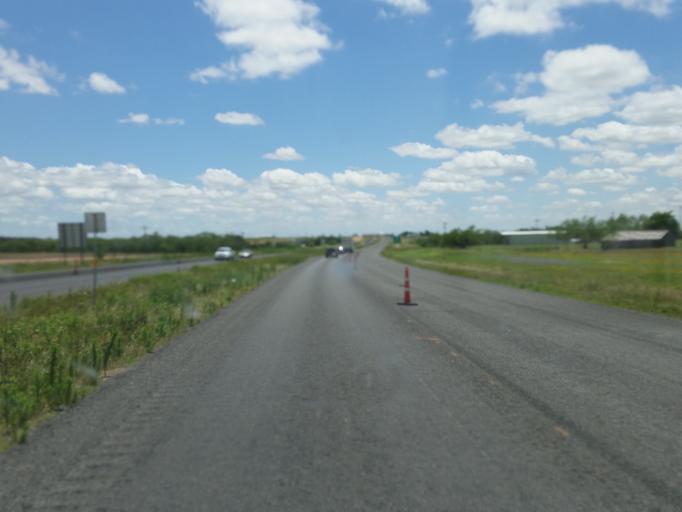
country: US
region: Texas
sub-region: Scurry County
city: Snyder
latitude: 32.7211
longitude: -100.8845
